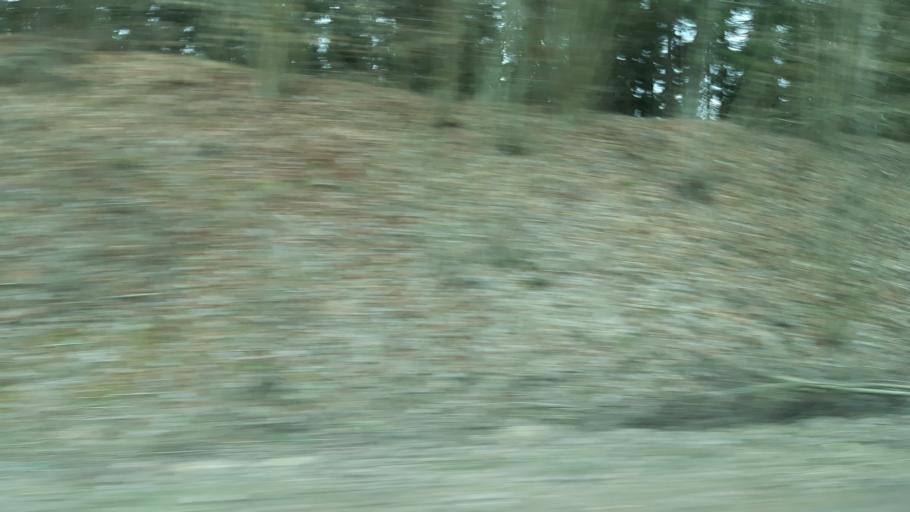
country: PL
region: Podlasie
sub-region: Suwalki
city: Suwalki
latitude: 54.2809
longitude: 22.9469
